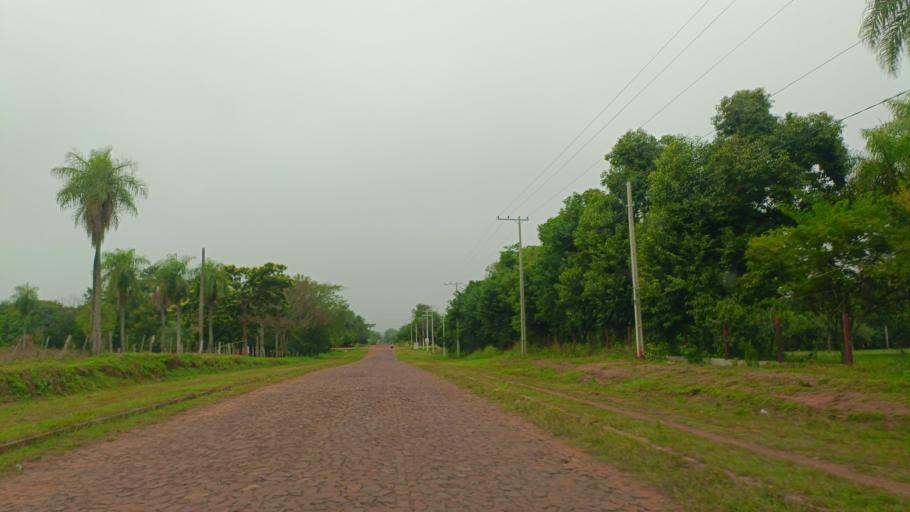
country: PY
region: Misiones
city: Santa Maria
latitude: -26.8619
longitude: -57.0231
